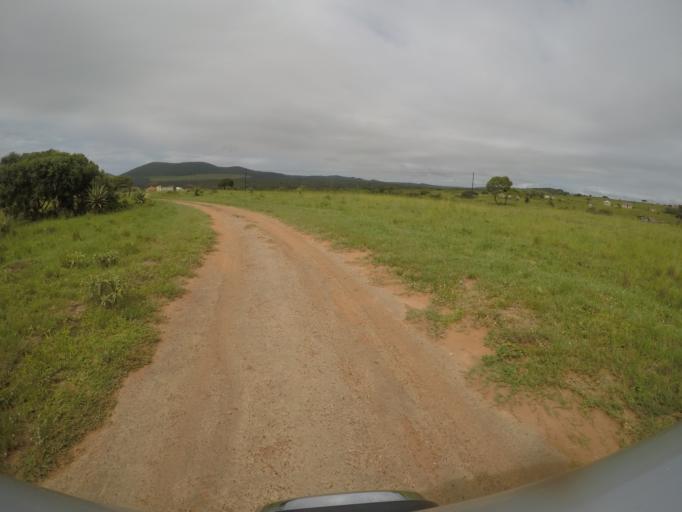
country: ZA
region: KwaZulu-Natal
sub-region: uThungulu District Municipality
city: Empangeni
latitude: -28.6139
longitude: 31.8454
